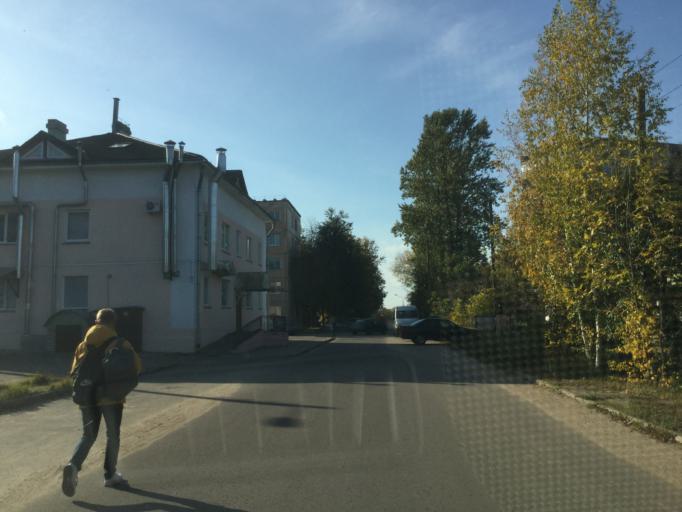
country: BY
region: Vitebsk
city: Vitebsk
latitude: 55.1881
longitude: 30.2359
